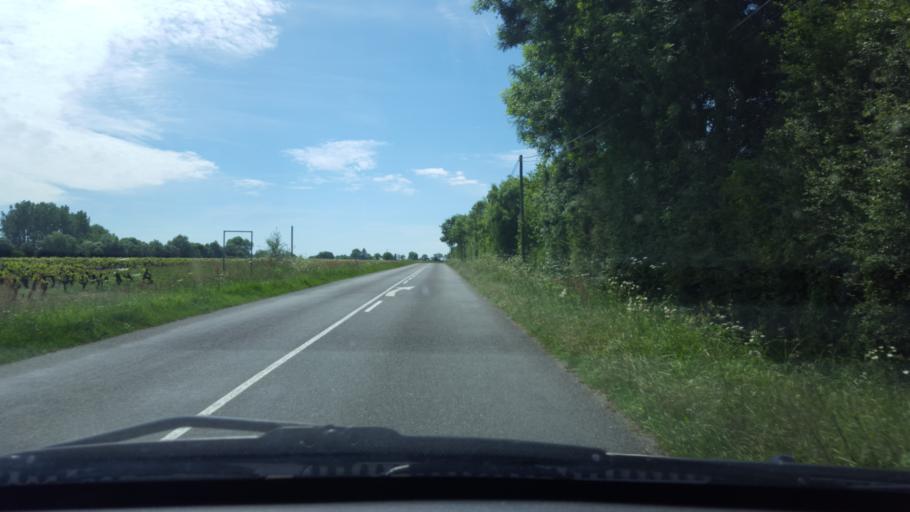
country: FR
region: Pays de la Loire
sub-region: Departement de la Loire-Atlantique
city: Saint-Philbert-de-Grand-Lieu
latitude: 47.0214
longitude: -1.6459
